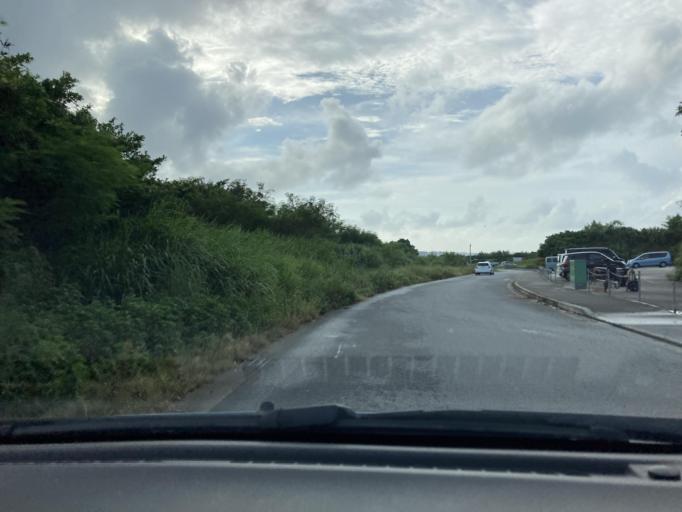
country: JP
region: Okinawa
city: Tomigusuku
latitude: 26.1757
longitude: 127.6426
